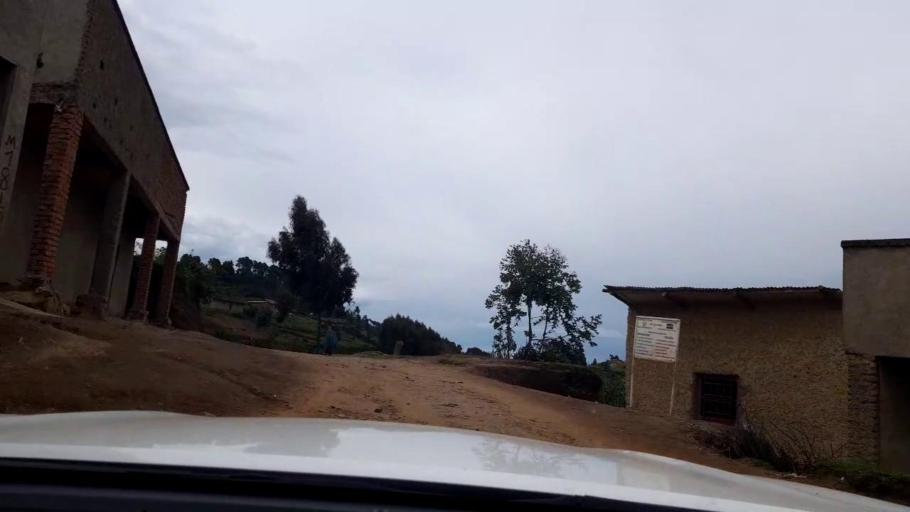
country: RW
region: Western Province
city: Kibuye
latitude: -1.8842
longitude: 29.4544
